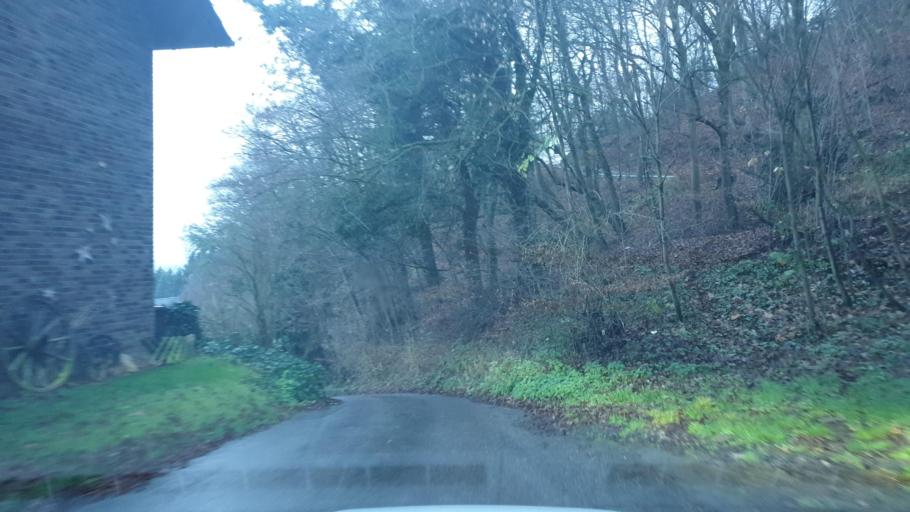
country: DE
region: North Rhine-Westphalia
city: Bad Oeynhausen
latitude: 52.2442
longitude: 8.8513
